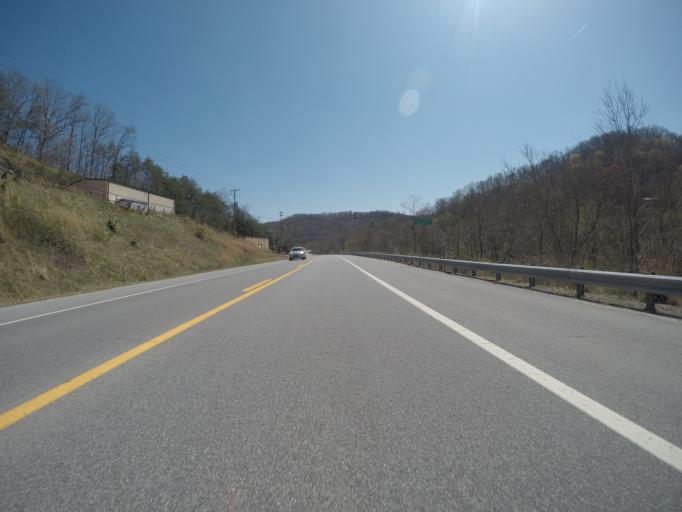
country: US
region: West Virginia
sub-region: Kanawha County
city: Pinch
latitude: 38.4106
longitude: -81.5440
